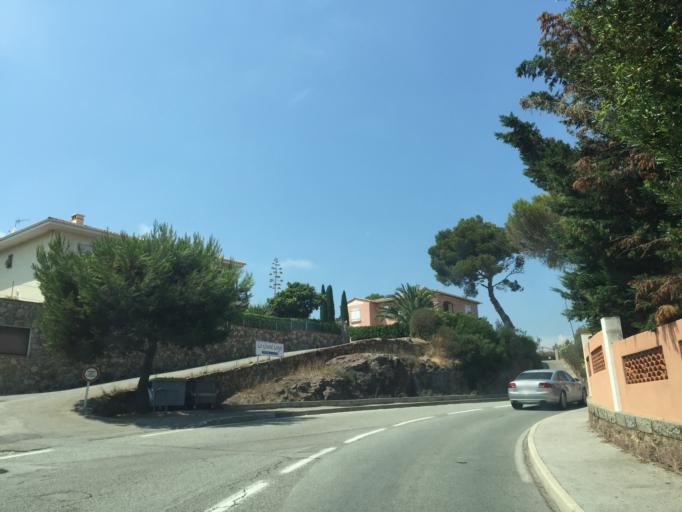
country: FR
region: Provence-Alpes-Cote d'Azur
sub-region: Departement du Var
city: Saint-Raphael
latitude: 43.4276
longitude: 6.8573
